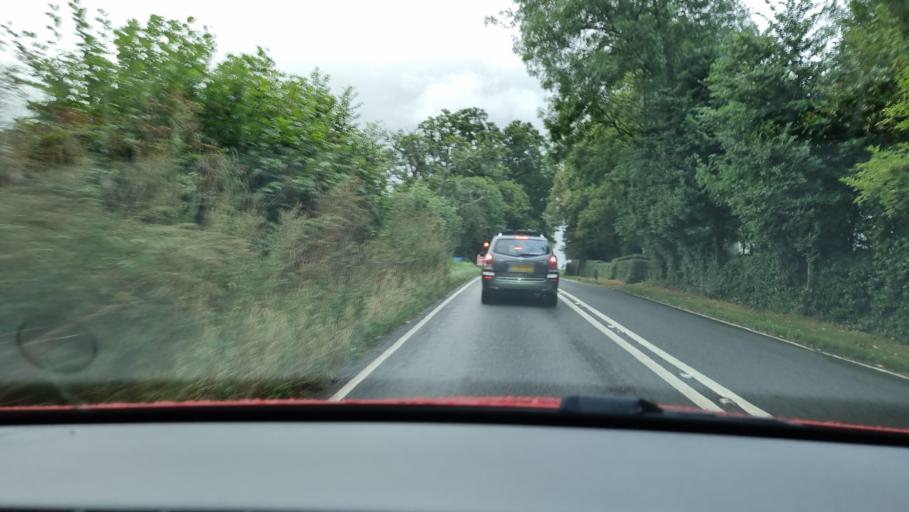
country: GB
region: England
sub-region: Hertfordshire
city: Berkhamsted
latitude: 51.7475
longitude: -0.5790
